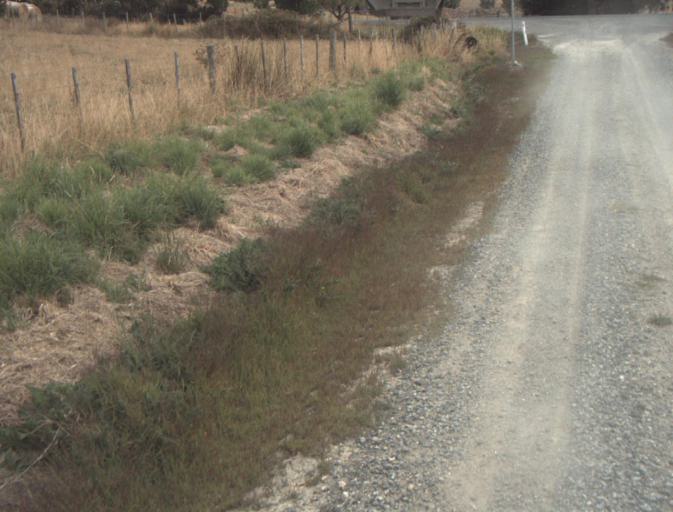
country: AU
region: Tasmania
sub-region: Launceston
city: Mayfield
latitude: -41.2097
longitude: 147.1097
